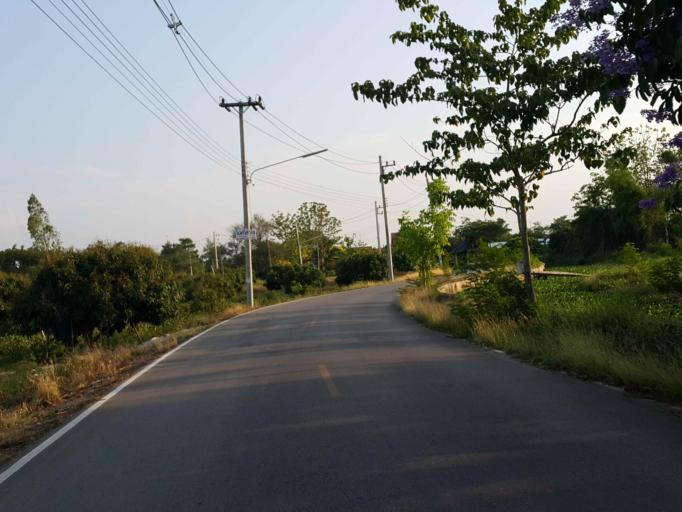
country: TH
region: Chiang Mai
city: Saraphi
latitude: 18.7147
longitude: 98.9792
